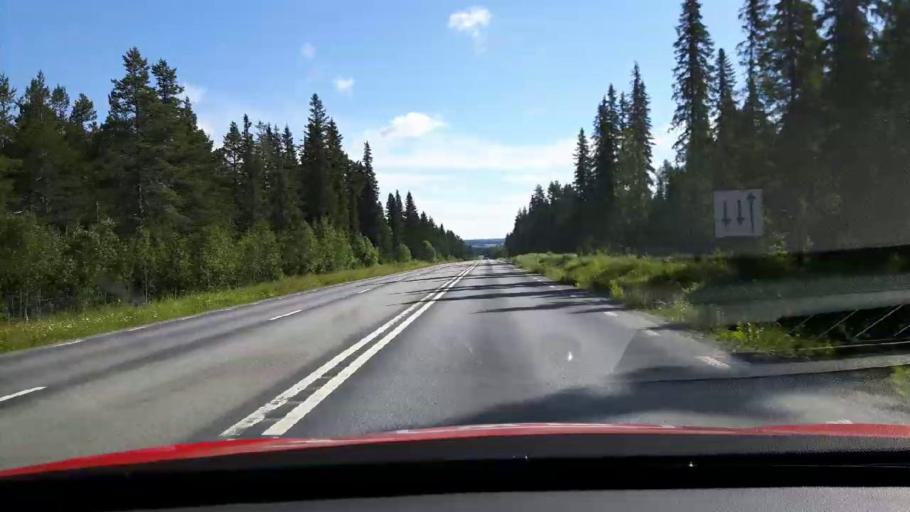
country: SE
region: Jaemtland
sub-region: OEstersunds Kommun
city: Lit
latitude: 63.2504
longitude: 14.8044
